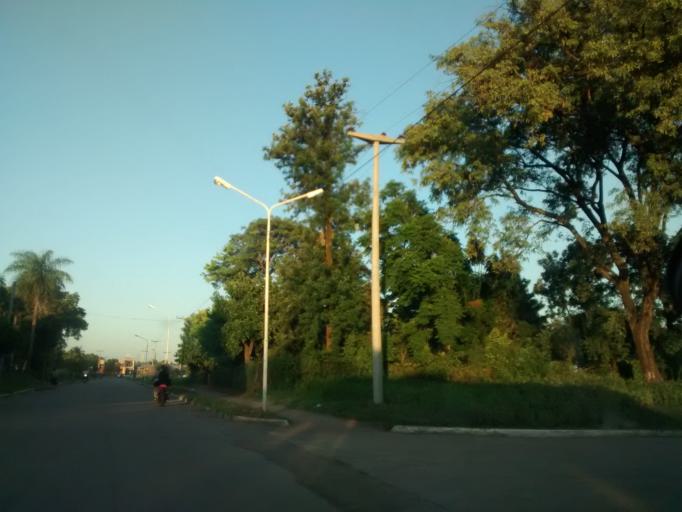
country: AR
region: Chaco
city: Fontana
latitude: -27.4148
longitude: -59.0308
